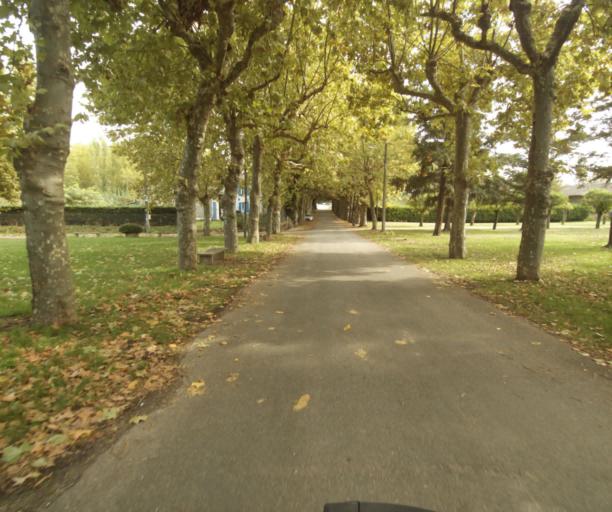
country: FR
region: Midi-Pyrenees
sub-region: Departement du Tarn-et-Garonne
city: Finhan
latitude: 43.9121
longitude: 1.2151
